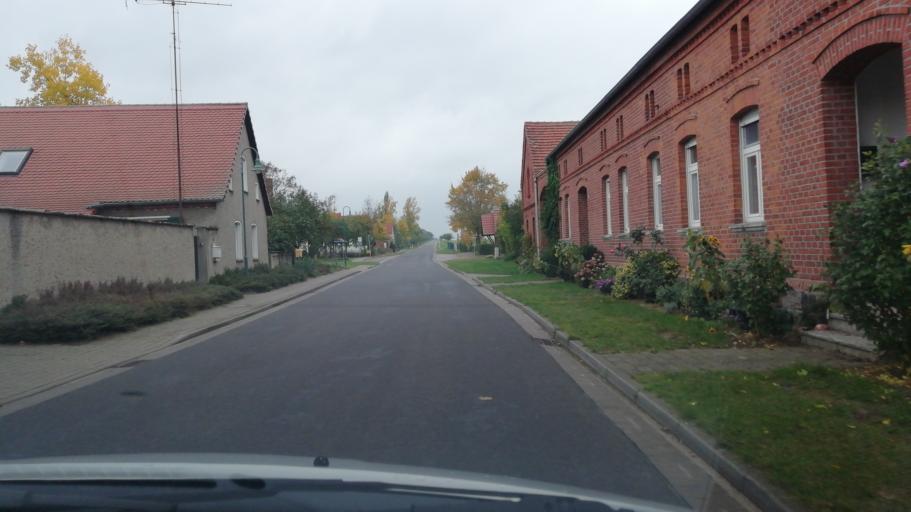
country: DE
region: Saxony-Anhalt
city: Luderitz
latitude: 52.4964
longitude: 11.7926
